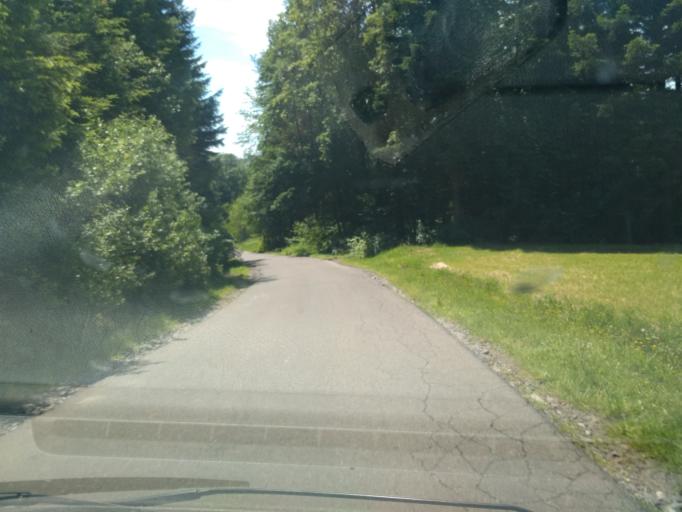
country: PL
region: Subcarpathian Voivodeship
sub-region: Powiat strzyzowski
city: Polomia
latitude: 49.9086
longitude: 21.9012
